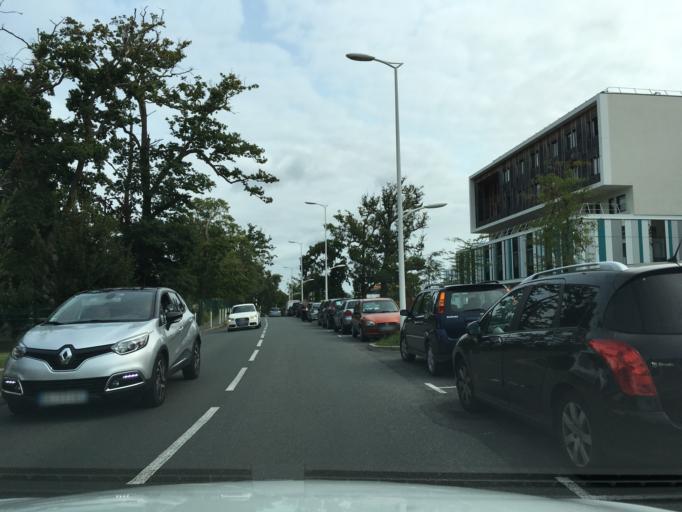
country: FR
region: Aquitaine
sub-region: Departement des Pyrenees-Atlantiques
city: Bayonne
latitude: 43.4794
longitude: -1.4539
